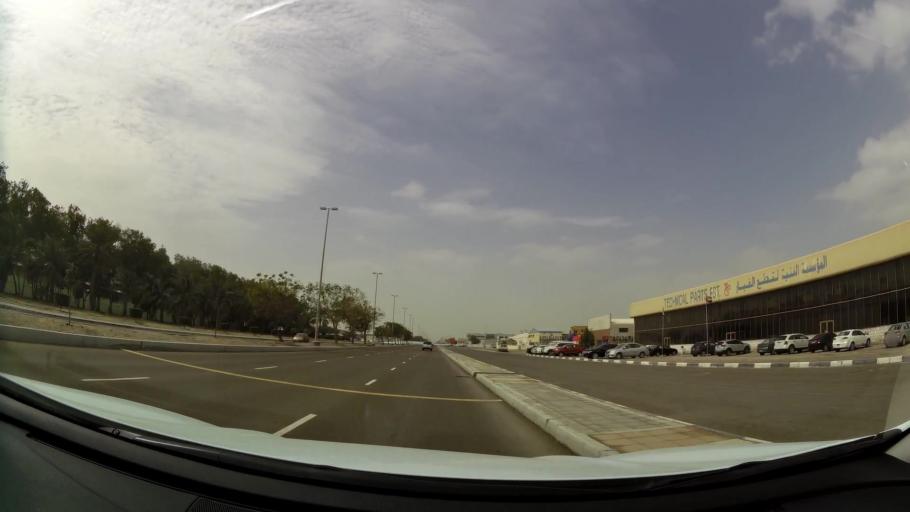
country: AE
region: Abu Dhabi
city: Abu Dhabi
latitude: 24.3827
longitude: 54.5182
